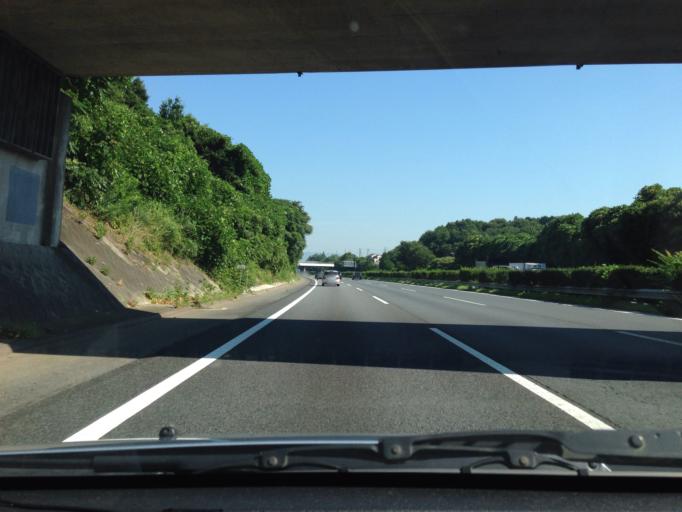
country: JP
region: Ibaraki
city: Naka
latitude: 36.0674
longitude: 140.1574
